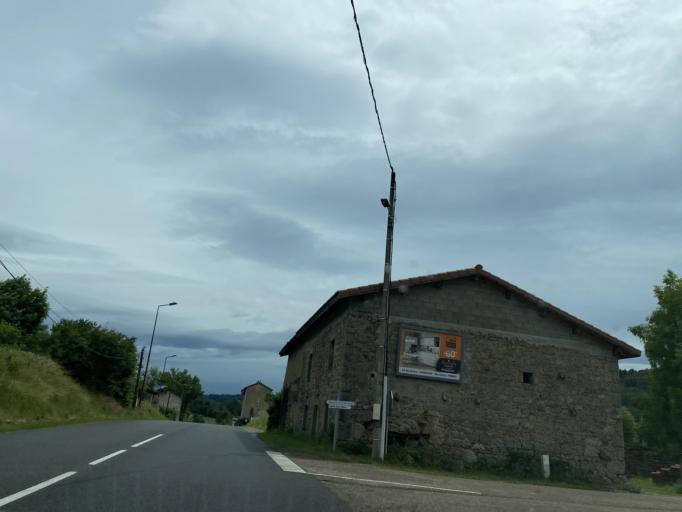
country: FR
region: Rhone-Alpes
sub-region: Departement de la Loire
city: Noiretable
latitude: 45.8156
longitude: 3.8221
